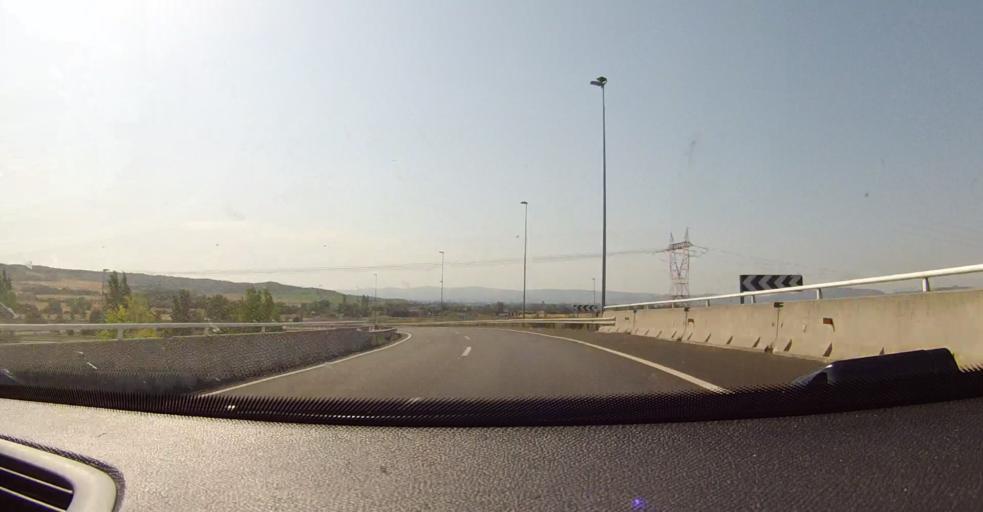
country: ES
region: Basque Country
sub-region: Provincia de Alava
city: Gasteiz / Vitoria
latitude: 42.9030
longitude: -2.7132
